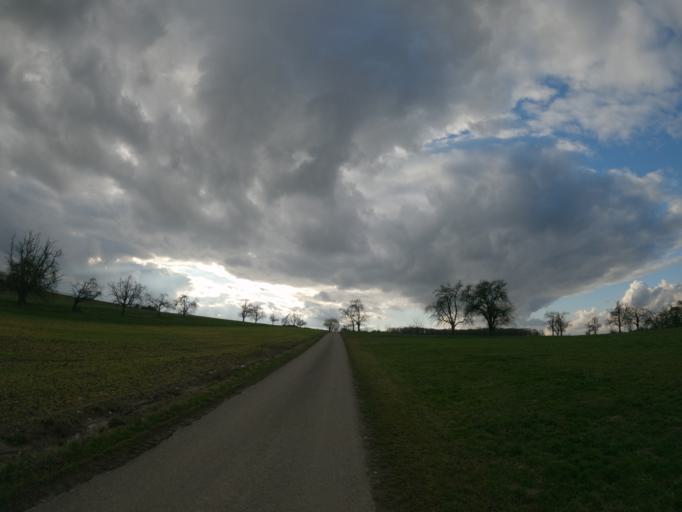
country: DE
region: Baden-Wuerttemberg
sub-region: Regierungsbezirk Stuttgart
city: Boll
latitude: 48.6562
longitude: 9.6123
